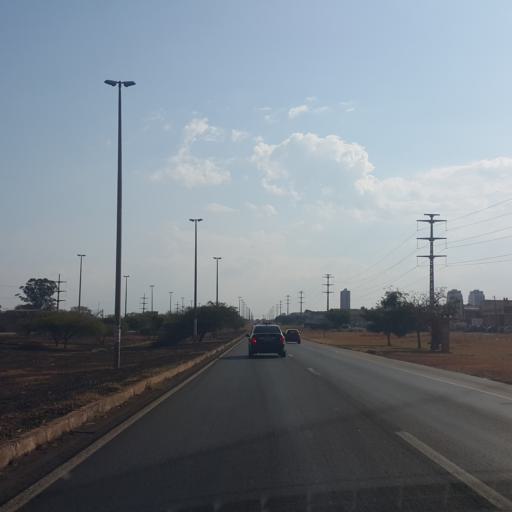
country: BR
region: Federal District
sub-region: Brasilia
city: Brasilia
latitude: -15.8859
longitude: -48.0725
